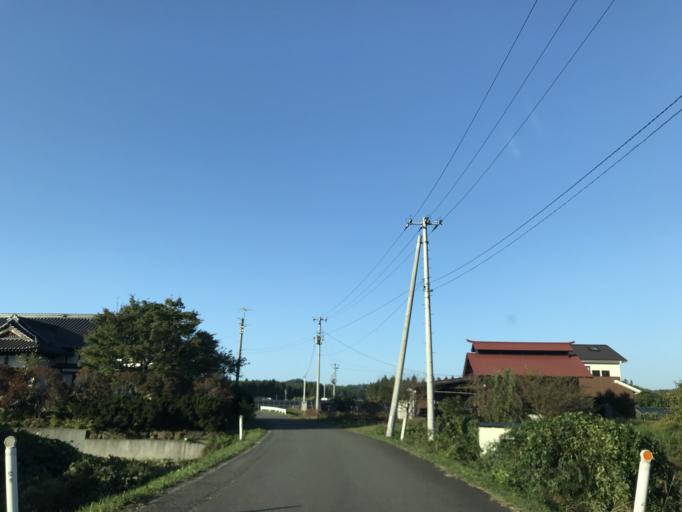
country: JP
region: Iwate
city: Ichinoseki
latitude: 38.9395
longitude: 141.0535
